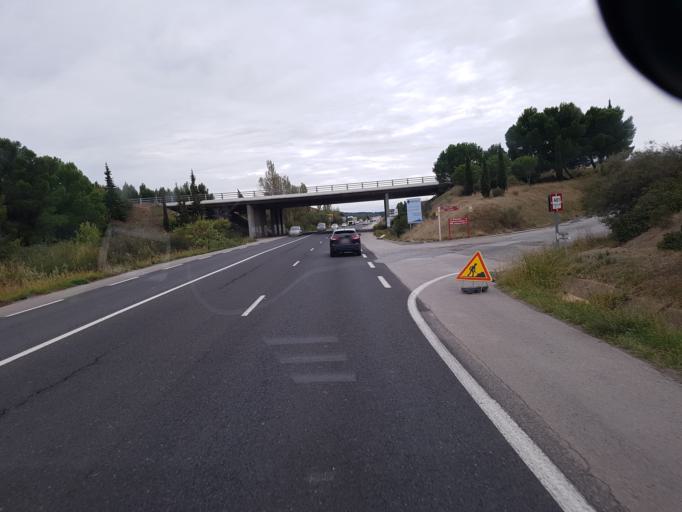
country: FR
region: Languedoc-Roussillon
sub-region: Departement de l'Aude
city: Narbonne
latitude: 43.1524
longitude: 2.9796
